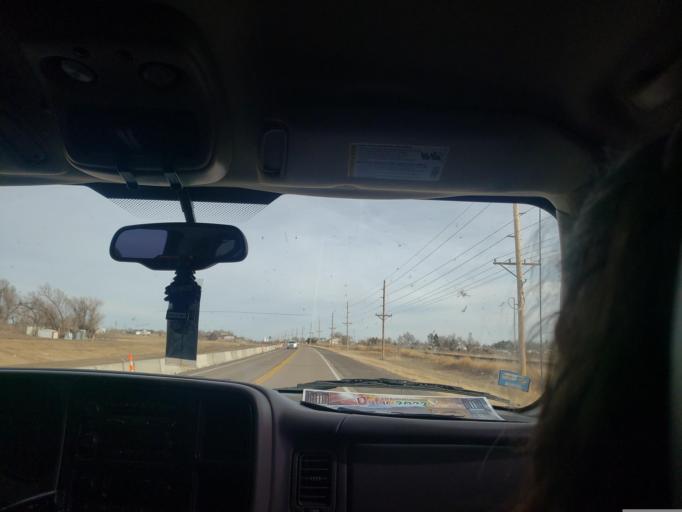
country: US
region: Kansas
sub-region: Ford County
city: Dodge City
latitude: 37.7559
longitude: -100.0777
